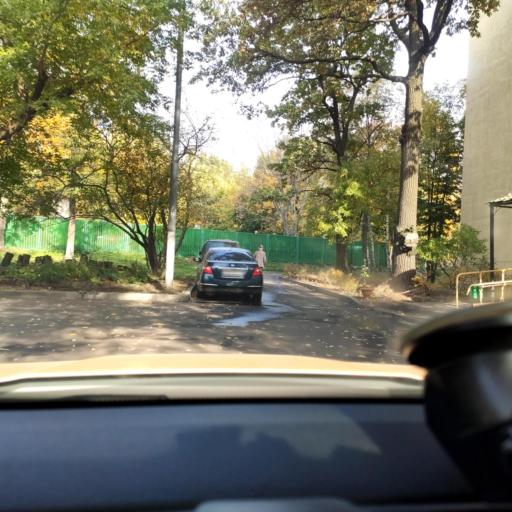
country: RU
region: Moscow
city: Ryazanskiy
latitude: 55.7300
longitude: 37.7670
